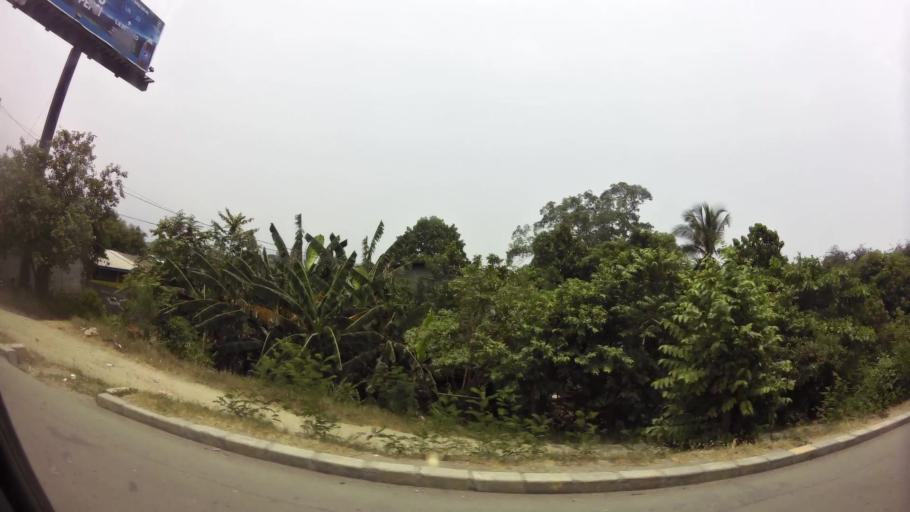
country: HN
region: Yoro
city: El Progreso
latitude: 15.4034
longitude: -87.8181
